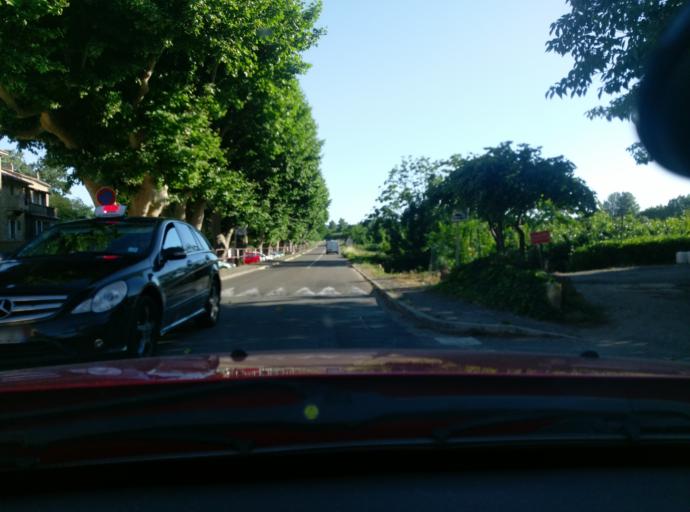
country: FR
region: Languedoc-Roussillon
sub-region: Departement du Gard
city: Remoulins
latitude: 43.9402
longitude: 4.5599
